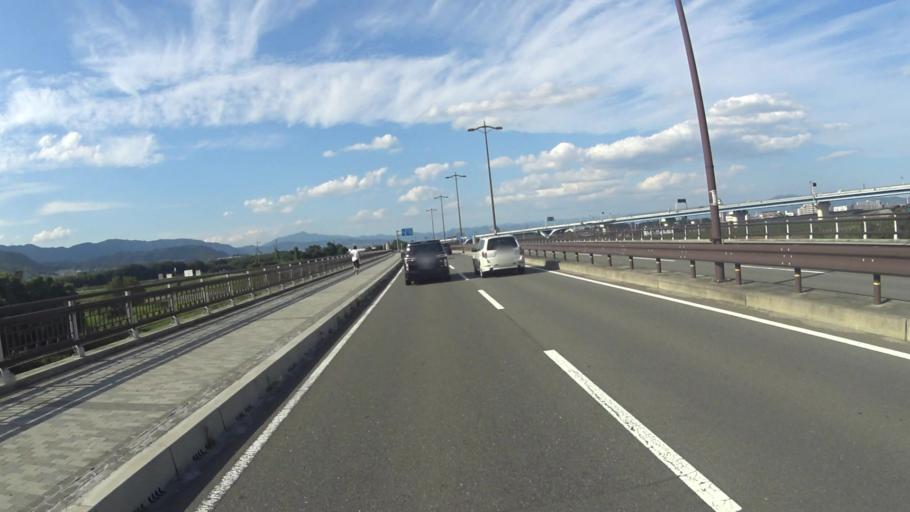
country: JP
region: Kyoto
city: Yawata
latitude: 34.8913
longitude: 135.7007
